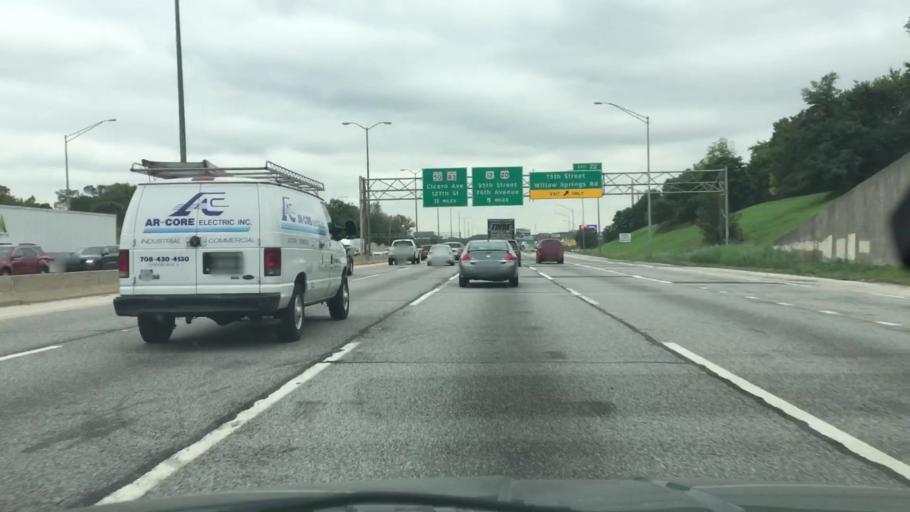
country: US
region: Illinois
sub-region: Cook County
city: Indian Head Park
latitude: 41.7573
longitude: -87.8820
